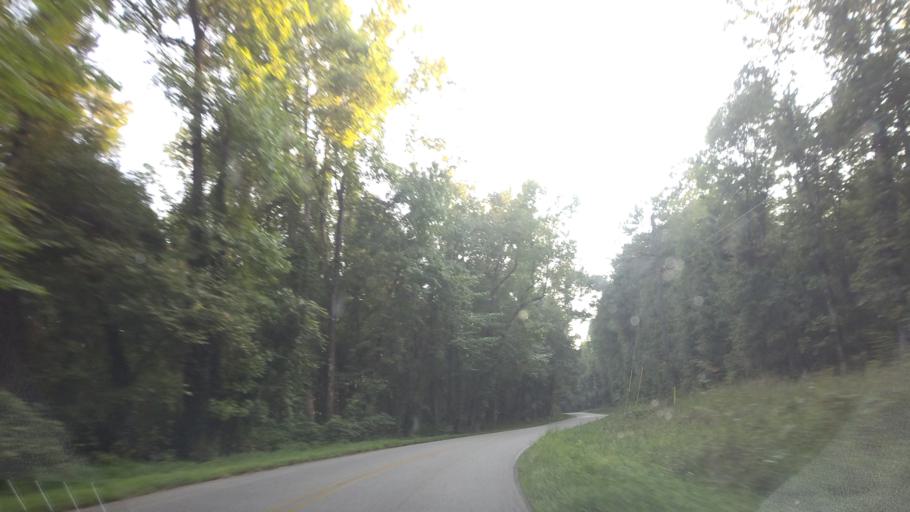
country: US
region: Georgia
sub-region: Bibb County
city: West Point
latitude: 32.9236
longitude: -83.8100
